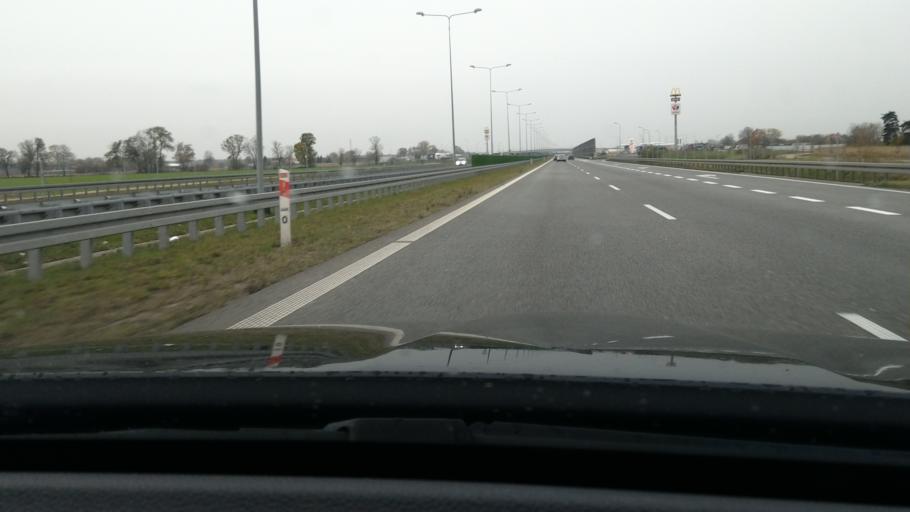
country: PL
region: Masovian Voivodeship
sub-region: Powiat pruszkowski
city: Brwinow
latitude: 52.1568
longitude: 20.6955
